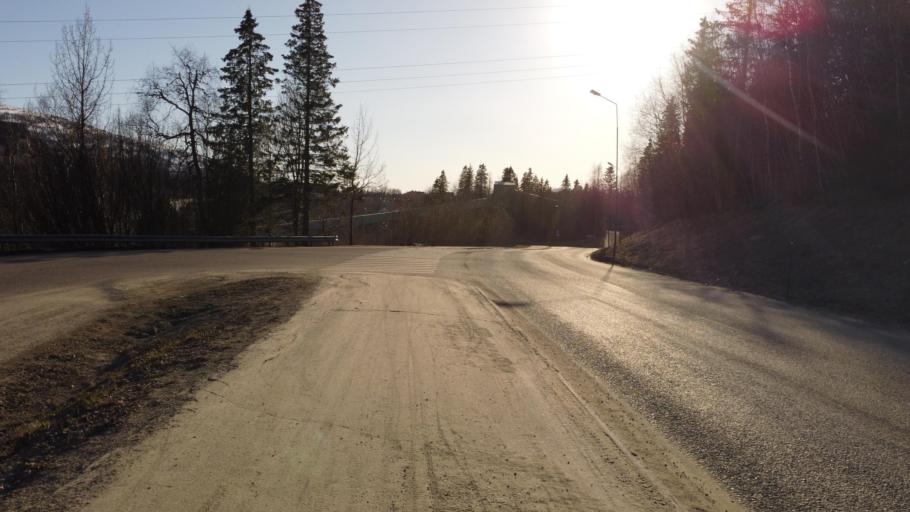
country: NO
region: Nordland
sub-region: Rana
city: Mo i Rana
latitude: 66.3179
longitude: 14.1761
